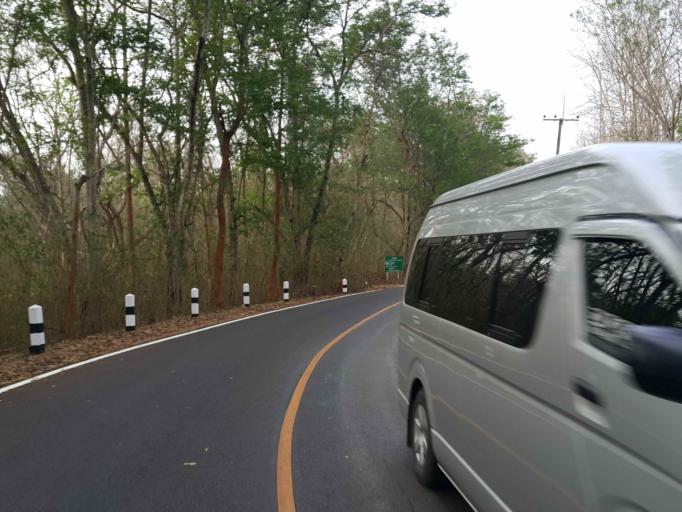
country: TH
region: Chiang Mai
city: Mae Taeng
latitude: 19.1630
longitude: 99.0304
